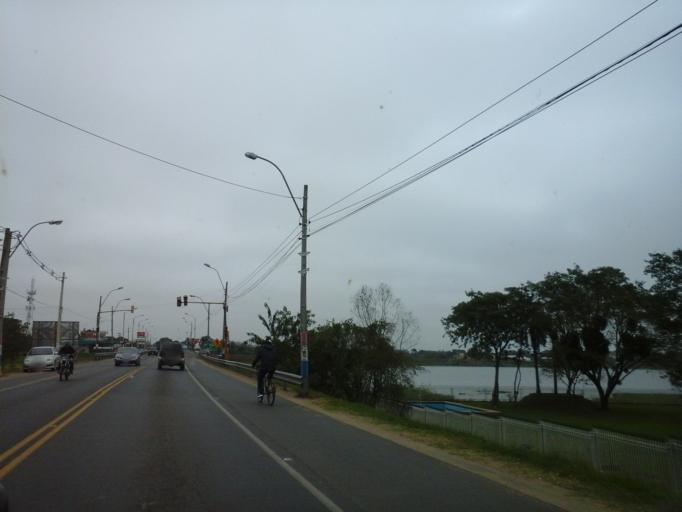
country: PY
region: Neembucu
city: Pilar
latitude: -26.8518
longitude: -58.2952
